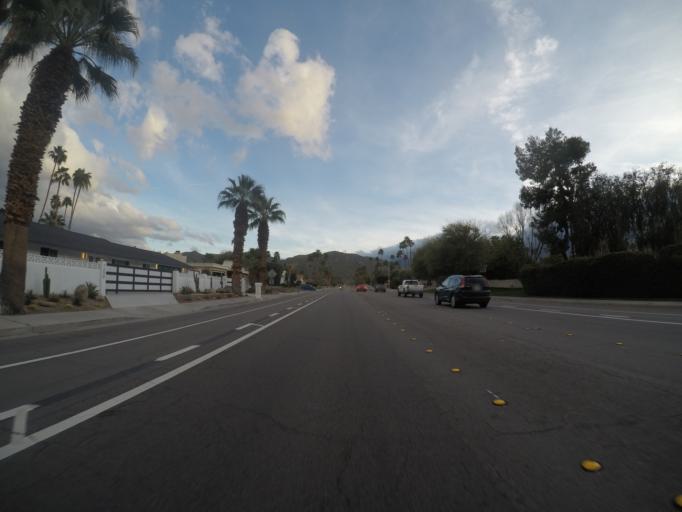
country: US
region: California
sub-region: Riverside County
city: Palm Springs
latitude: 33.8057
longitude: -116.5194
